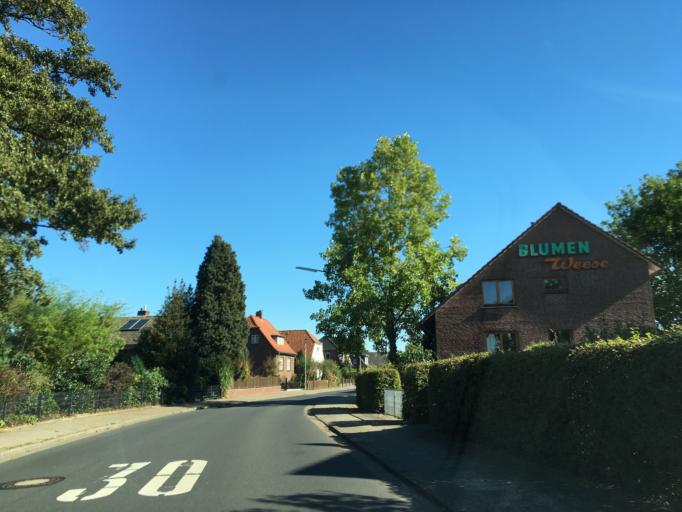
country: DE
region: Lower Saxony
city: Winsen
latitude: 53.3473
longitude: 10.2107
